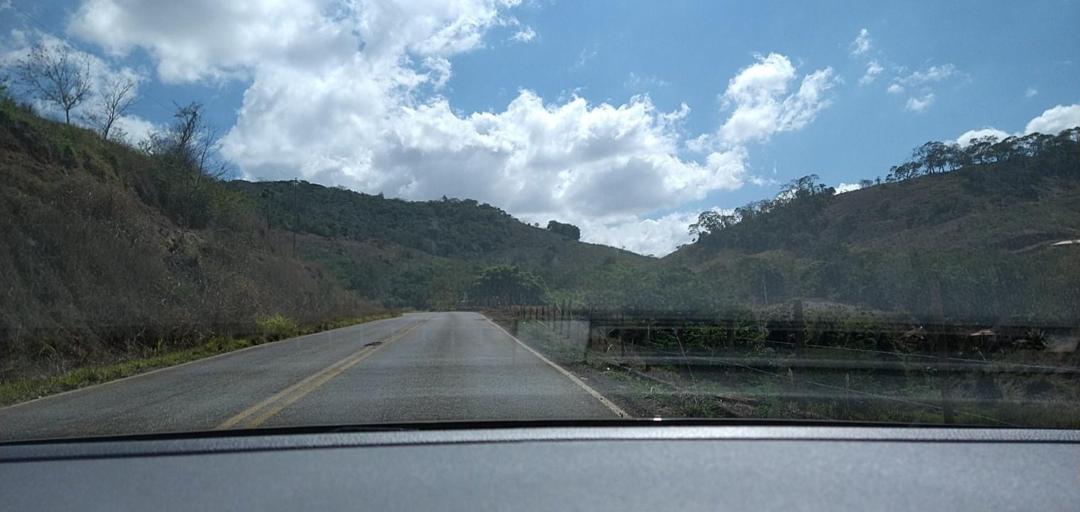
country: BR
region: Minas Gerais
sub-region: Ponte Nova
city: Ponte Nova
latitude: -20.2766
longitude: -42.9016
